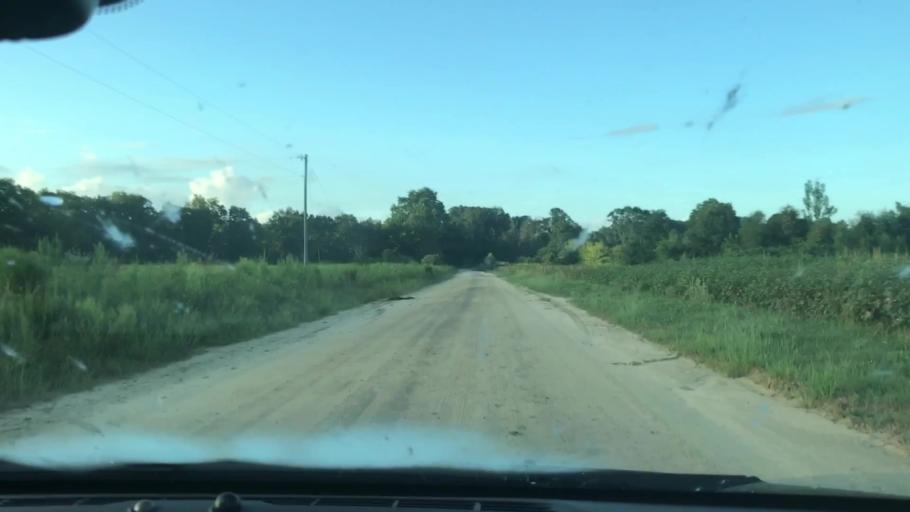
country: US
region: Georgia
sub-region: Clay County
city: Fort Gaines
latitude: 31.7185
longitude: -85.0668
